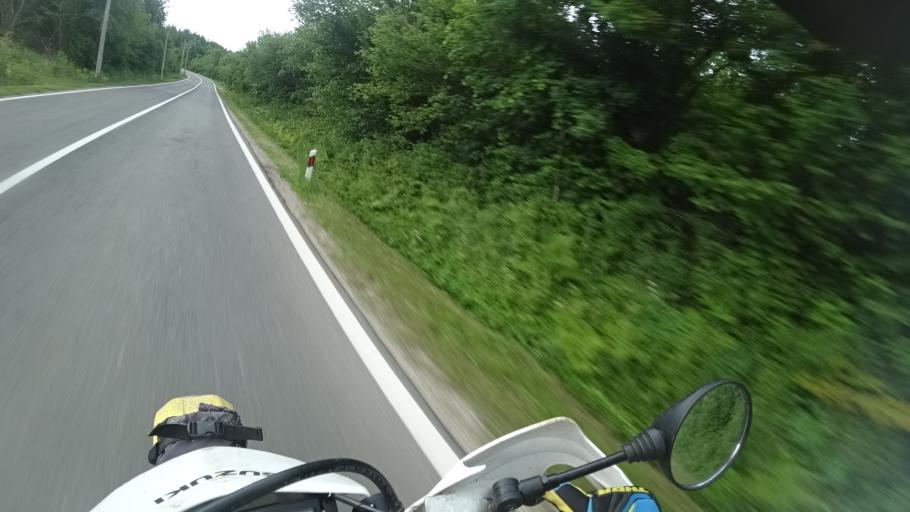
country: HR
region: Licko-Senjska
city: Gospic
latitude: 44.4933
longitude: 15.4601
